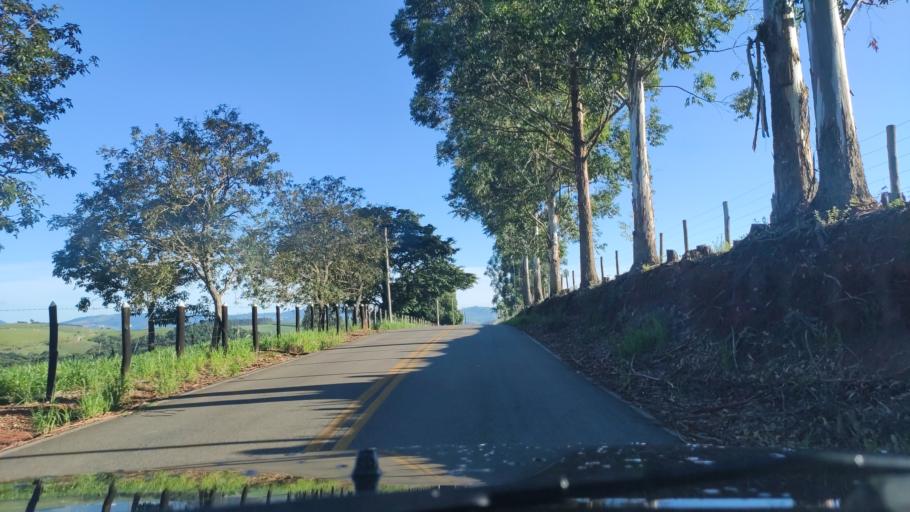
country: BR
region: Sao Paulo
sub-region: Serra Negra
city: Serra Negra
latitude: -22.5855
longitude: -46.6227
